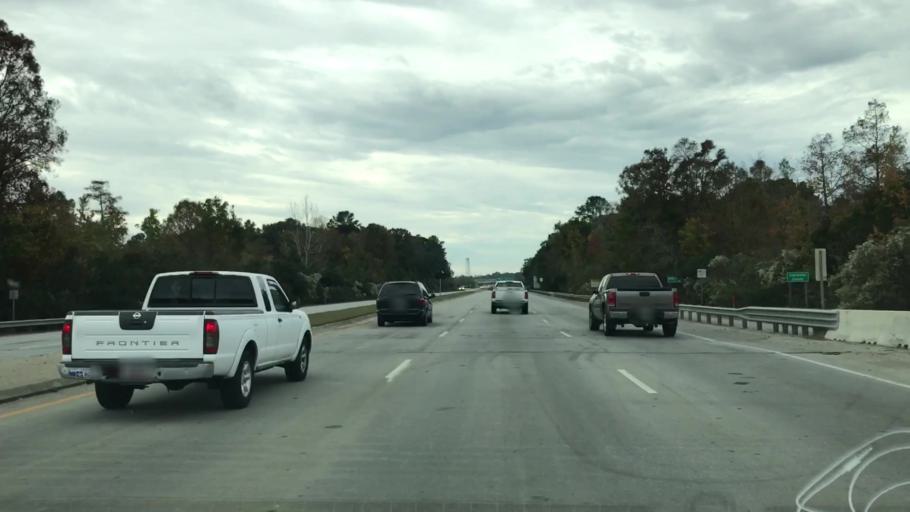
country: US
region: South Carolina
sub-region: Berkeley County
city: Goose Creek
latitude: 32.9843
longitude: -80.0418
